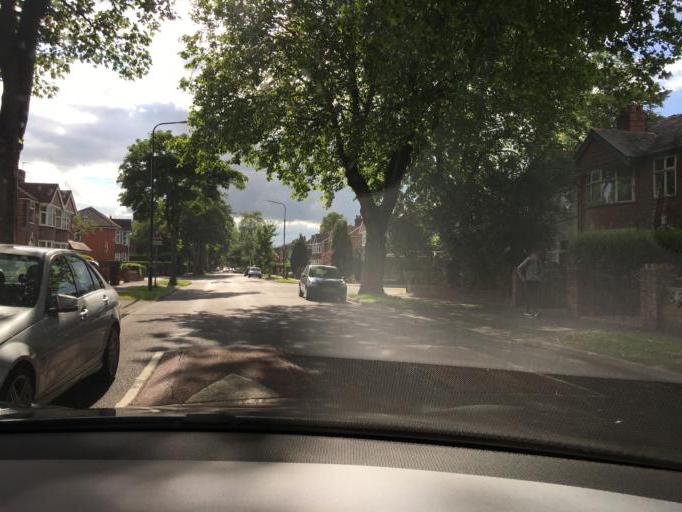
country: GB
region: England
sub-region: Trafford
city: Urmston
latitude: 53.4549
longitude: -2.3471
